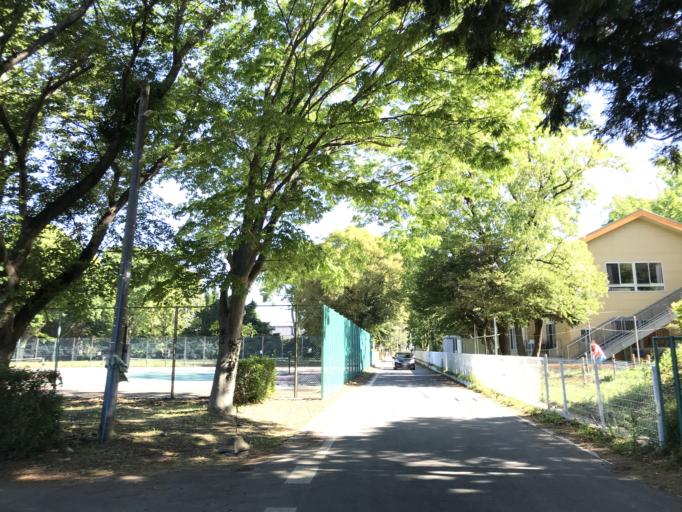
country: JP
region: Ibaraki
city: Tsukuba
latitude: 36.1093
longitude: 140.0660
